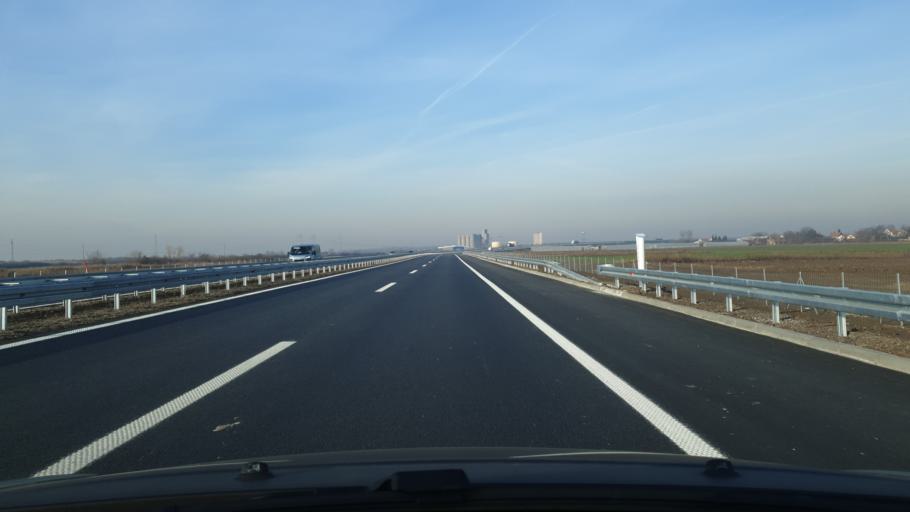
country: RS
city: Boljevci
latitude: 44.7570
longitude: 20.2476
